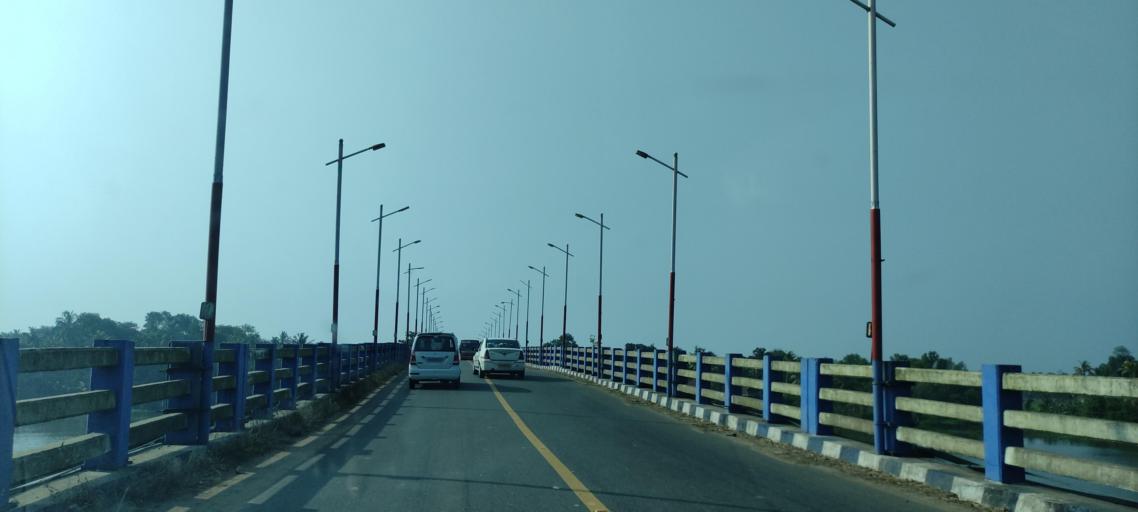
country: IN
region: Kerala
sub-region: Kottayam
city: Changanacheri
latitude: 9.3701
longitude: 76.4254
